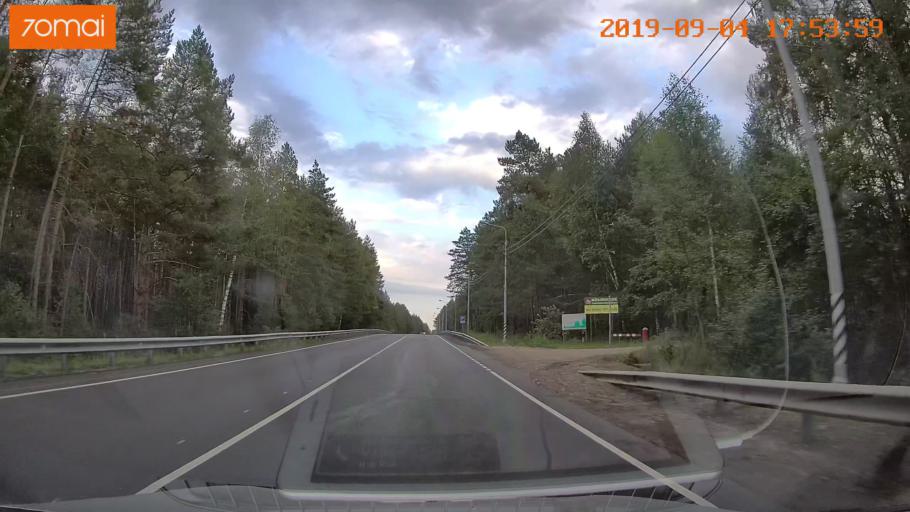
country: RU
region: Moskovskaya
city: Imeni Tsyurupy
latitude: 55.5131
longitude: 38.7333
